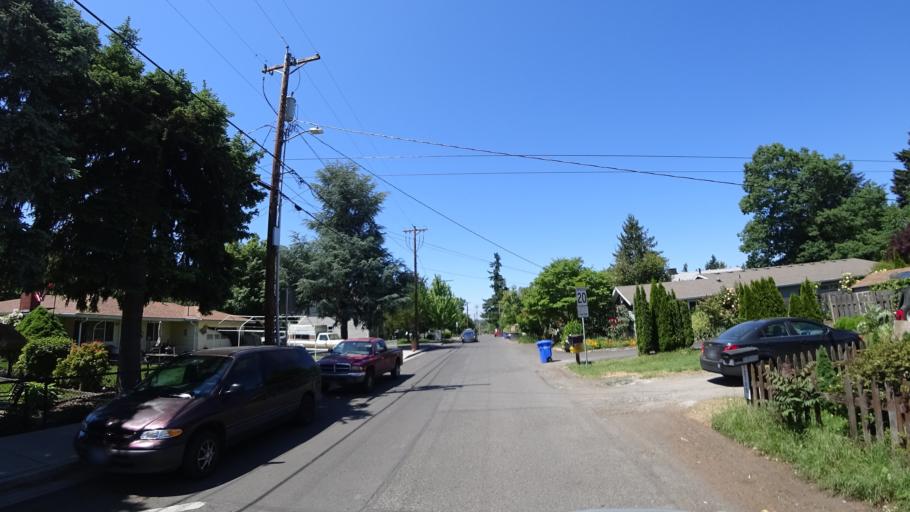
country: US
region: Oregon
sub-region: Clackamas County
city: Happy Valley
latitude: 45.4801
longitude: -122.5330
